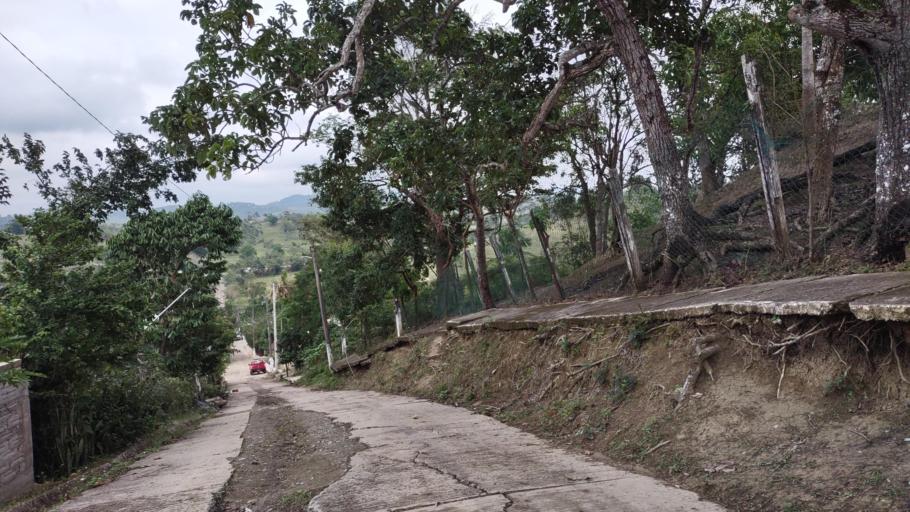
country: MX
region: Veracruz
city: Coatzintla
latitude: 20.4568
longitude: -97.4210
